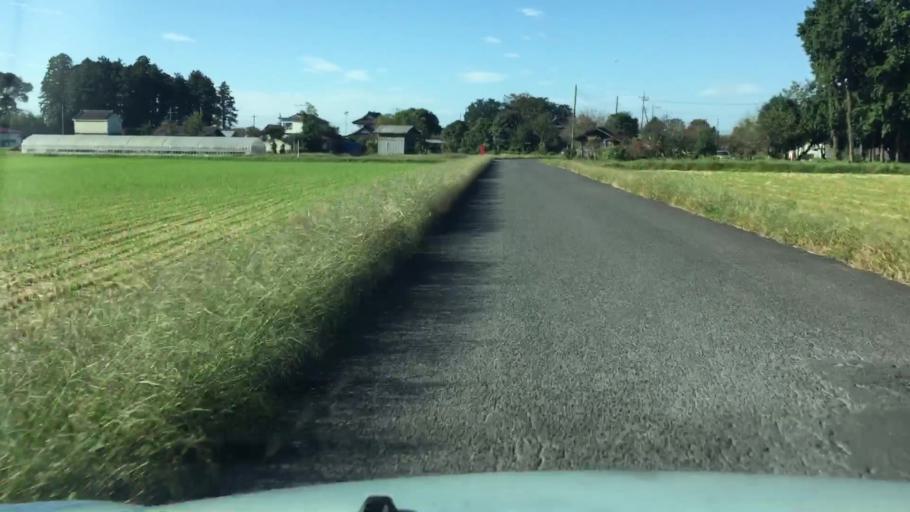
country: JP
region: Tochigi
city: Ujiie
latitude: 36.6935
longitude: 140.0090
